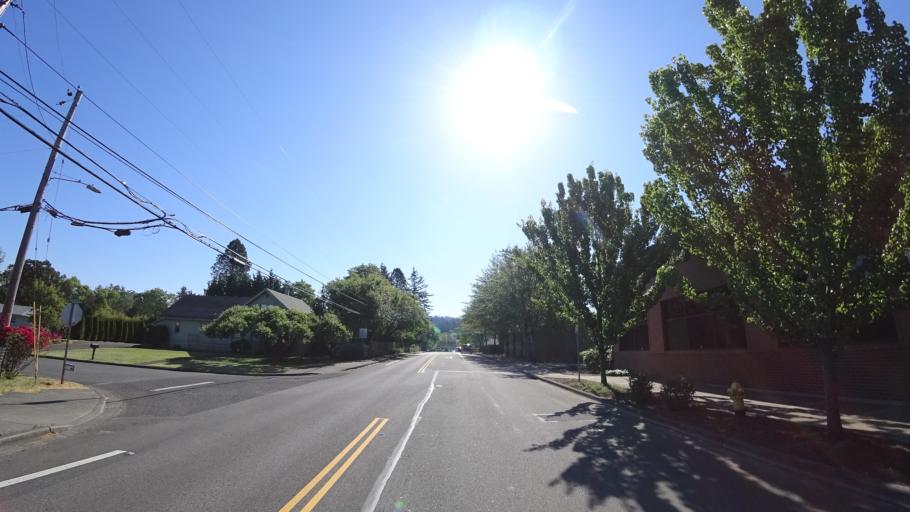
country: US
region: Oregon
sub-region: Washington County
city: Metzger
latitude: 45.4380
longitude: -122.7590
